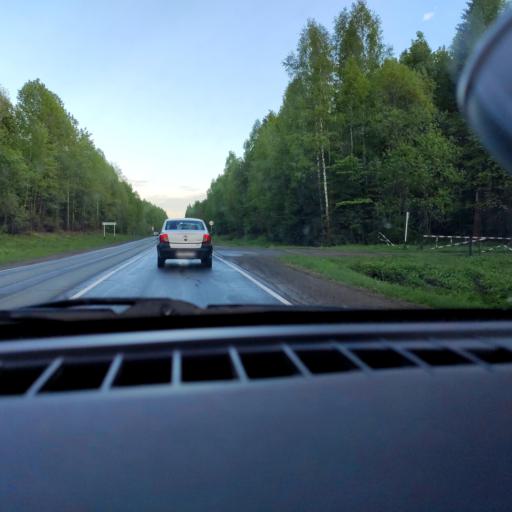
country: RU
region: Perm
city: Perm
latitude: 58.1517
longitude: 56.2557
